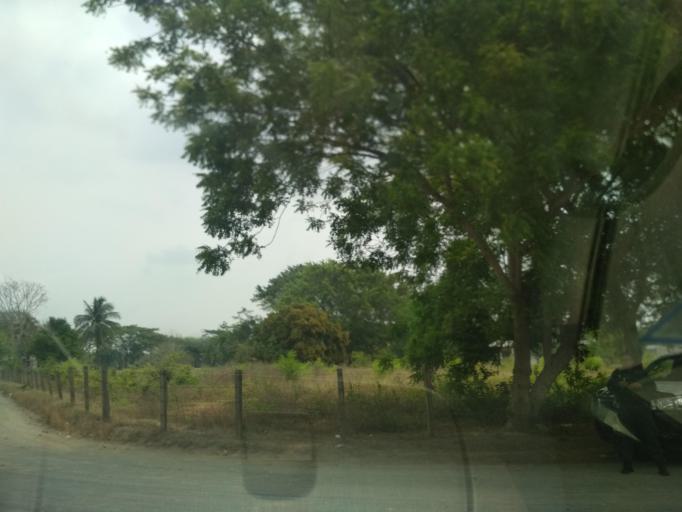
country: MX
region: Veracruz
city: Paso del Toro
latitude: 19.0218
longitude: -96.1504
